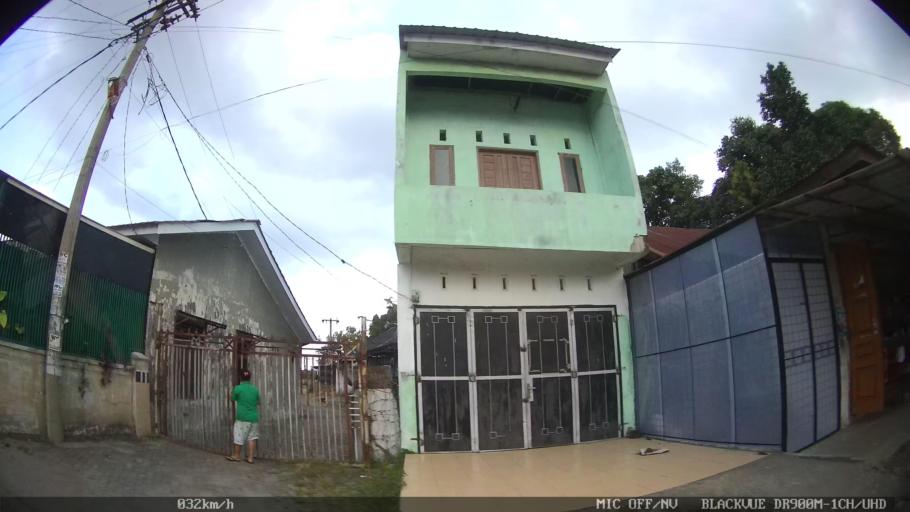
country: ID
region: North Sumatra
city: Medan
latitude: 3.5927
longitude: 98.7423
